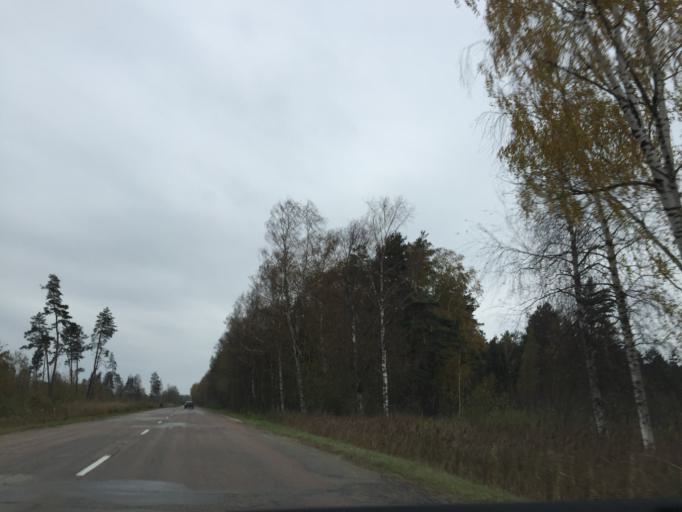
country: LV
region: Marupe
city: Marupe
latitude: 56.8629
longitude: 24.0599
